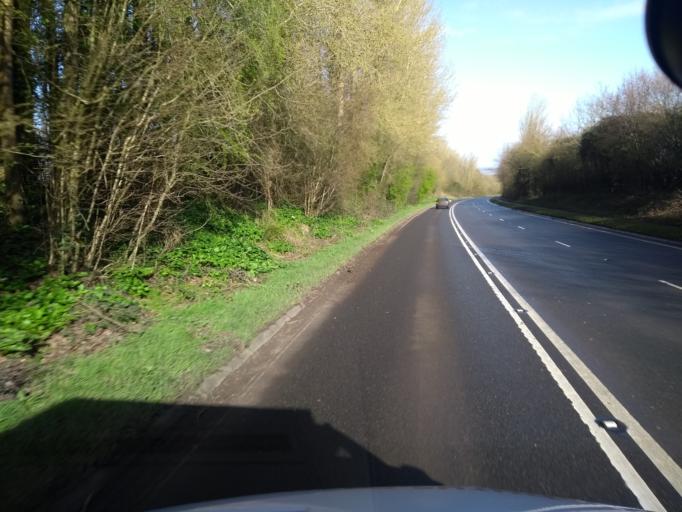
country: GB
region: England
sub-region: Somerset
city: Yeovil
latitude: 50.9584
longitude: -2.6506
